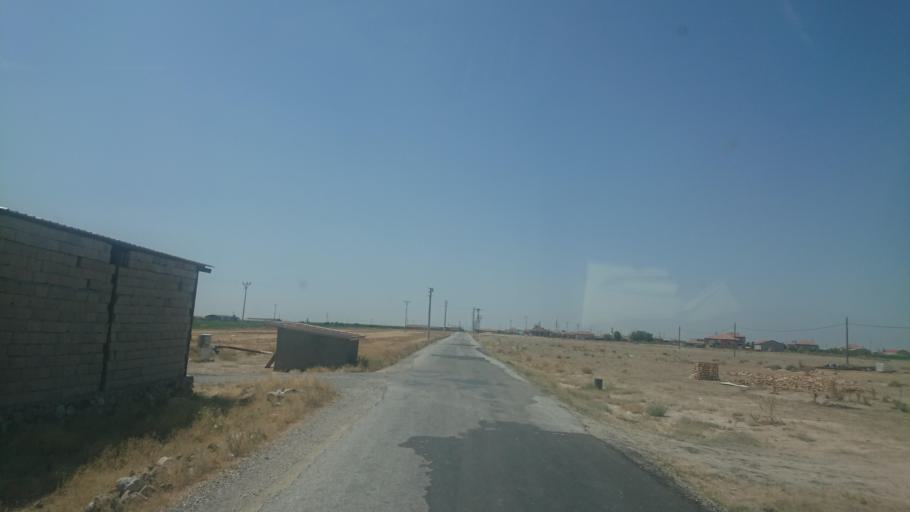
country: TR
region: Aksaray
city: Yesilova
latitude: 38.2918
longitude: 33.7209
